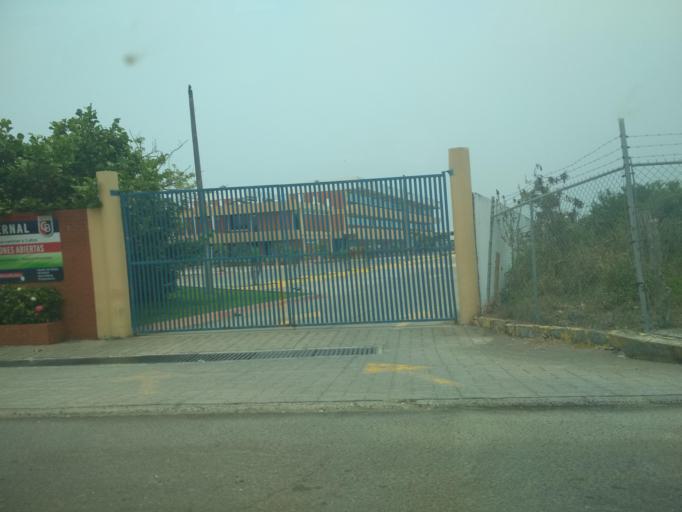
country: MX
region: Veracruz
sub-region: Alvarado
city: Playa de la Libertad
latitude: 19.0584
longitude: -96.0697
